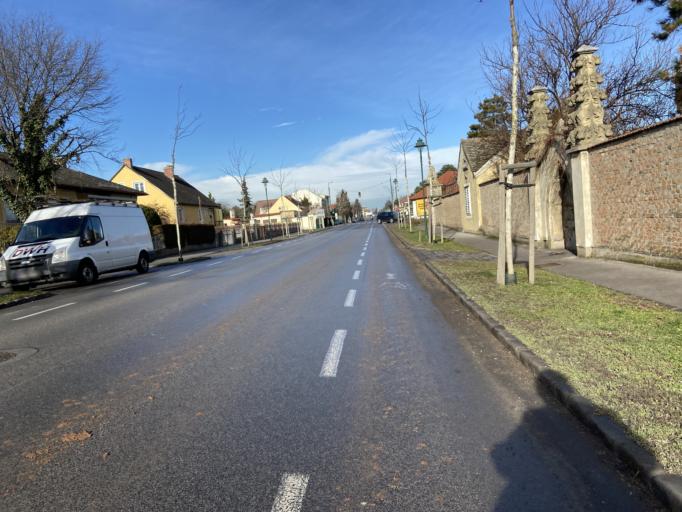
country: AT
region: Lower Austria
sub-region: Politischer Bezirk Modling
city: Laxenburg
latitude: 48.0709
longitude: 16.3550
